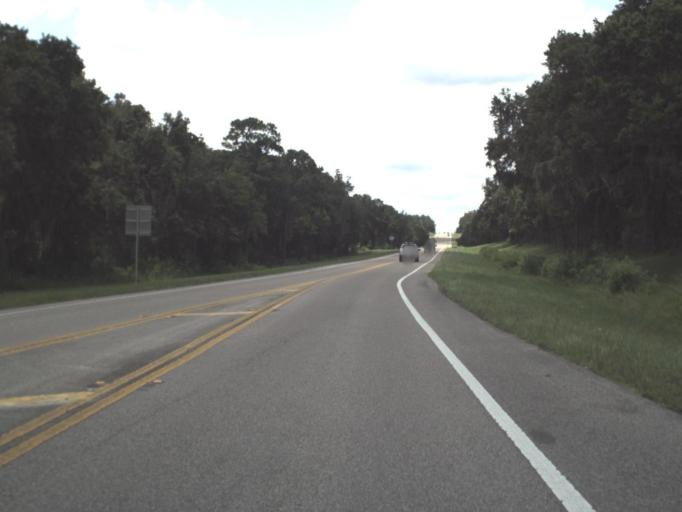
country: US
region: Florida
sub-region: Hernando County
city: North Brooksville
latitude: 28.5821
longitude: -82.4003
